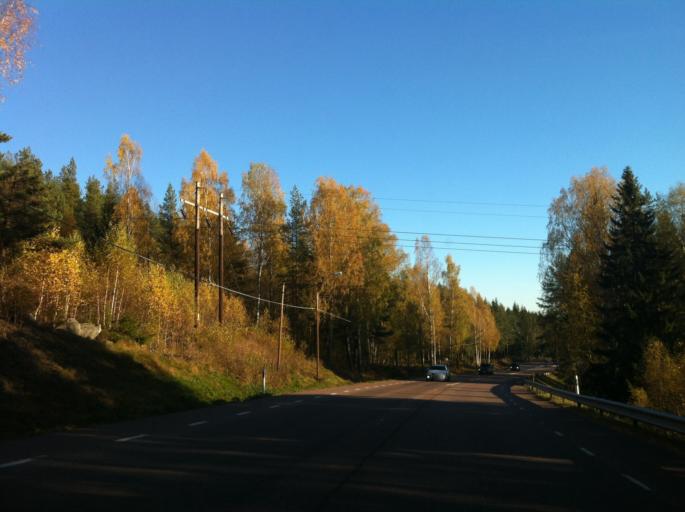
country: SE
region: Dalarna
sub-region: Faluns Kommun
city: Grycksbo
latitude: 60.6888
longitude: 15.4924
